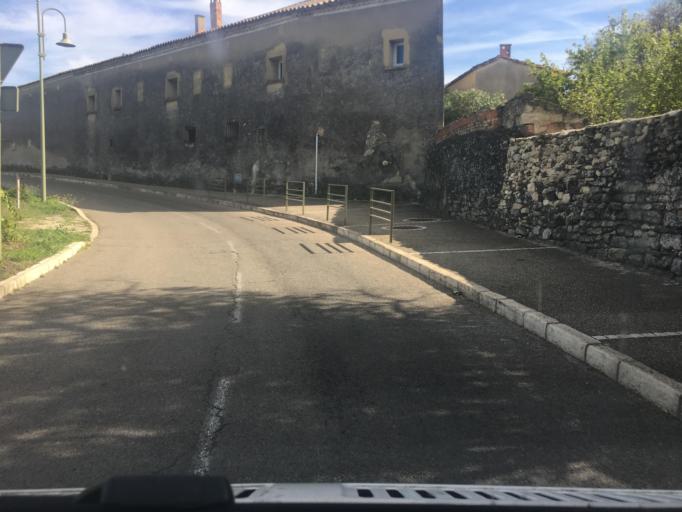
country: FR
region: Languedoc-Roussillon
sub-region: Departement du Gard
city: Uzes
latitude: 44.0173
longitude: 4.4199
